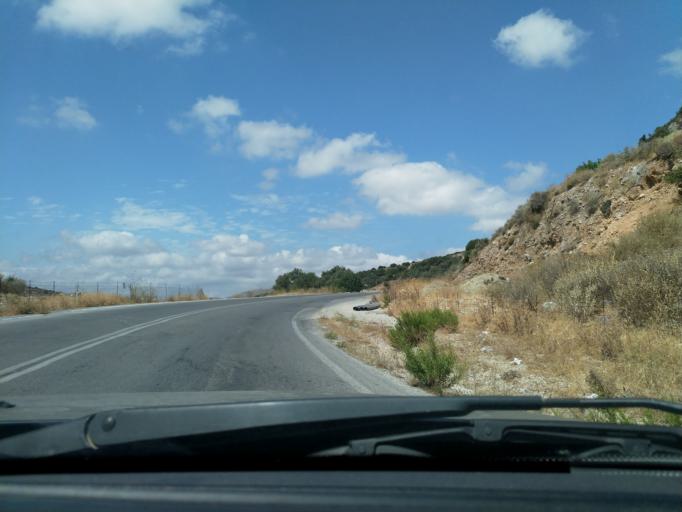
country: GR
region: Crete
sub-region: Nomos Rethymnis
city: Agia Foteini
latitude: 35.2052
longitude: 24.5420
